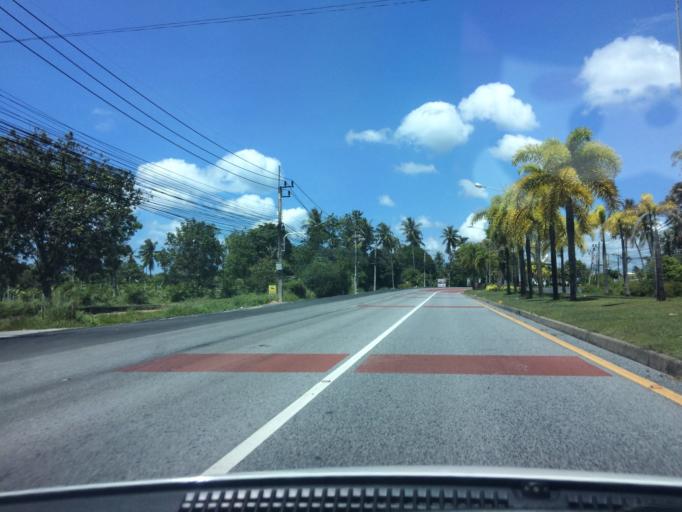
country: TH
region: Phuket
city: Thalang
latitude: 8.1719
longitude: 98.2988
